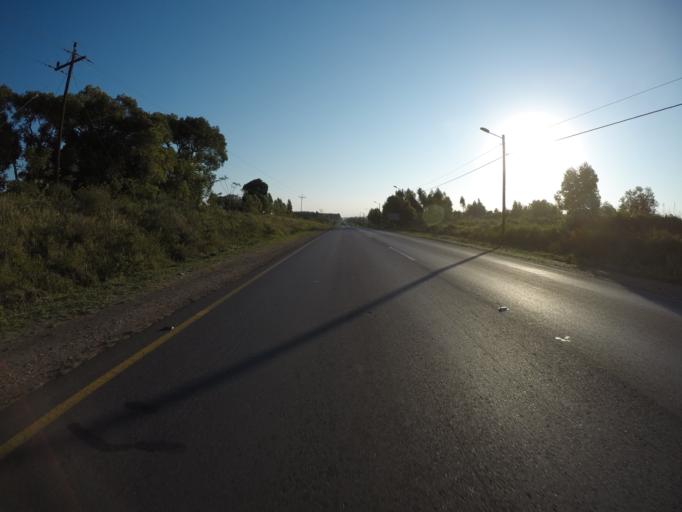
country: ZA
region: KwaZulu-Natal
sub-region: uThungulu District Municipality
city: KwaMbonambi
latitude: -28.6831
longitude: 32.1998
